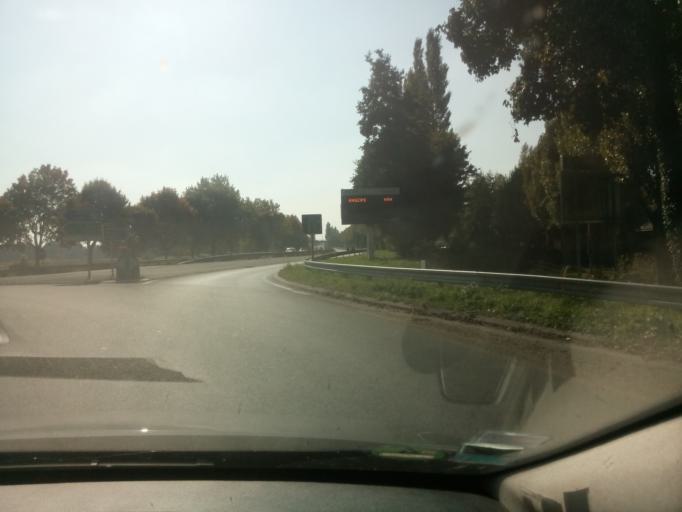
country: FR
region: Pays de la Loire
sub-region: Departement de Maine-et-Loire
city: Pellouailles-les-Vignes
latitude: 47.5254
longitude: -0.4280
